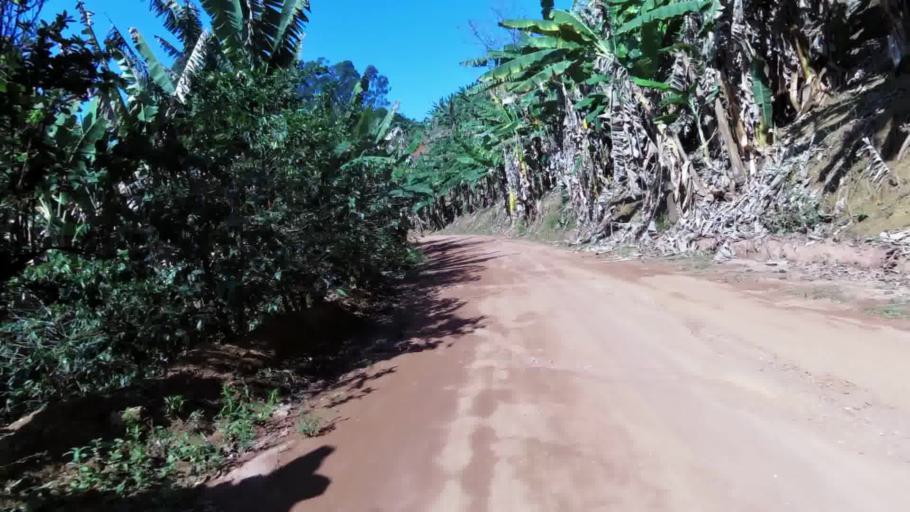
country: BR
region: Espirito Santo
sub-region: Alfredo Chaves
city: Alfredo Chaves
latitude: -20.5643
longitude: -40.7742
